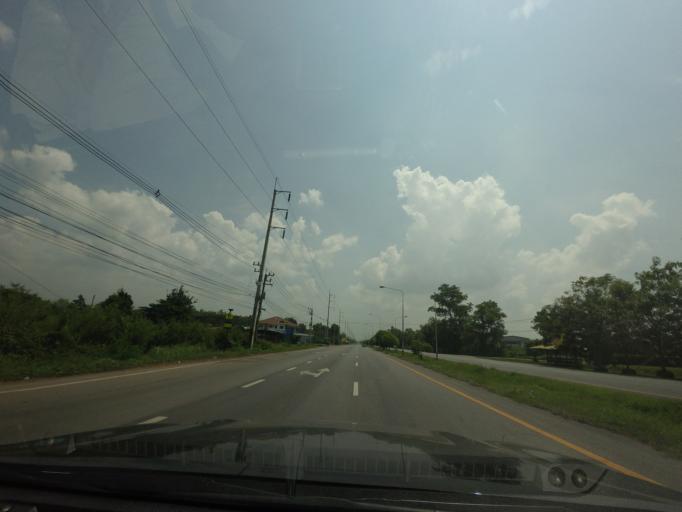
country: TH
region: Uttaradit
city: Uttaradit
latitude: 17.5799
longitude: 100.1440
